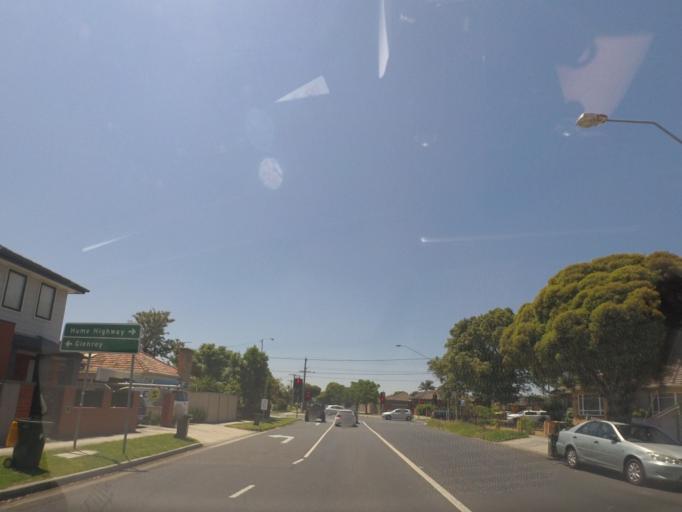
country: AU
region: Victoria
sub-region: Moreland
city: Hadfield
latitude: -37.7174
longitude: 144.9407
